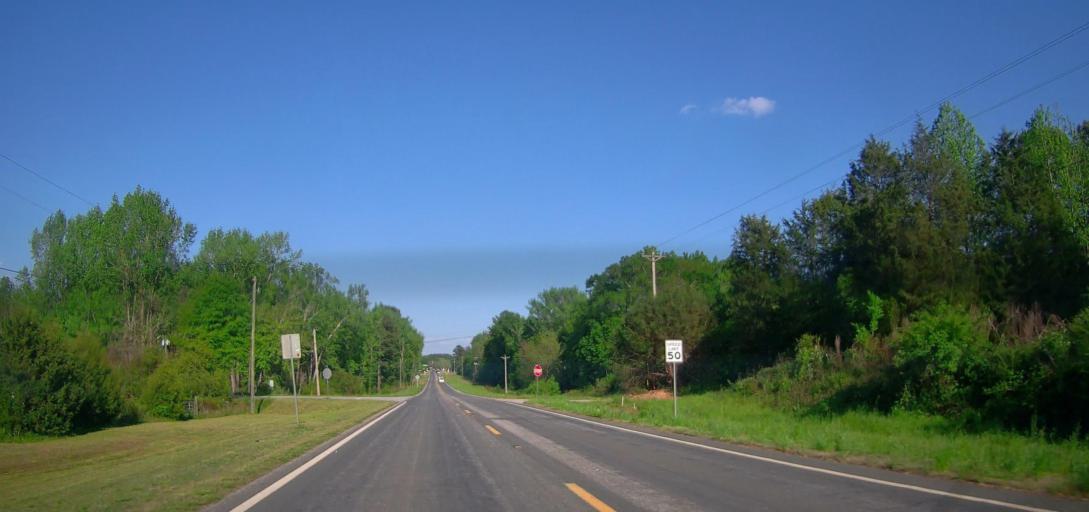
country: US
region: Georgia
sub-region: Walton County
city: Social Circle
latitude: 33.6230
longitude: -83.6178
